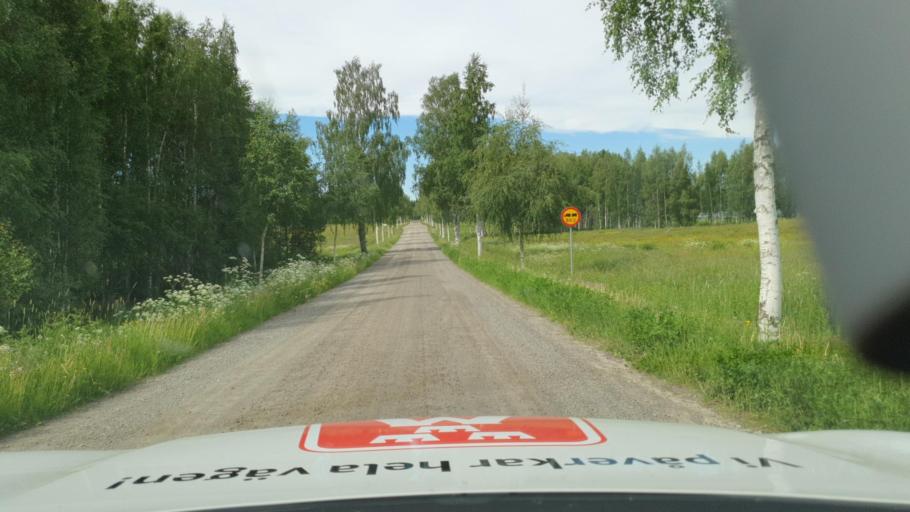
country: SE
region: Vaesterbotten
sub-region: Skelleftea Kommun
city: Burtraesk
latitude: 64.4559
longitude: 20.4777
